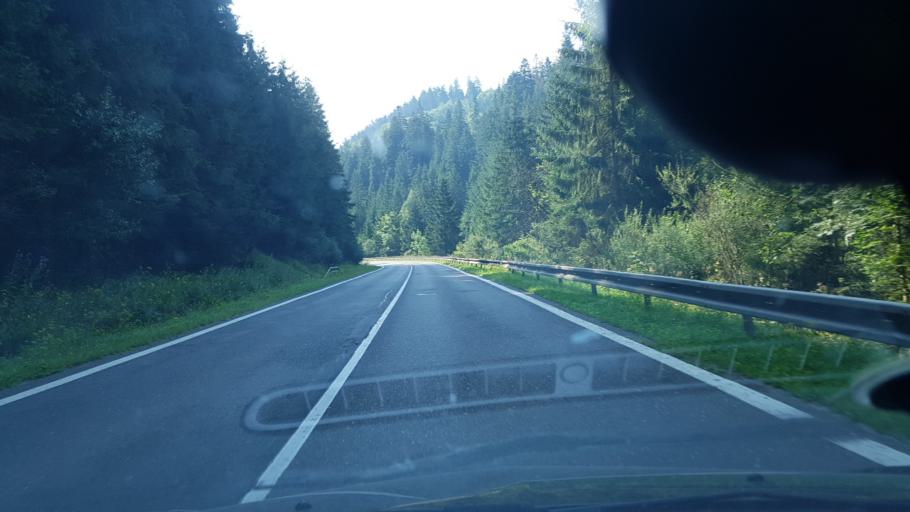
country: SK
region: Zilinsky
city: Ruzomberok
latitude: 49.1289
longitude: 19.2883
